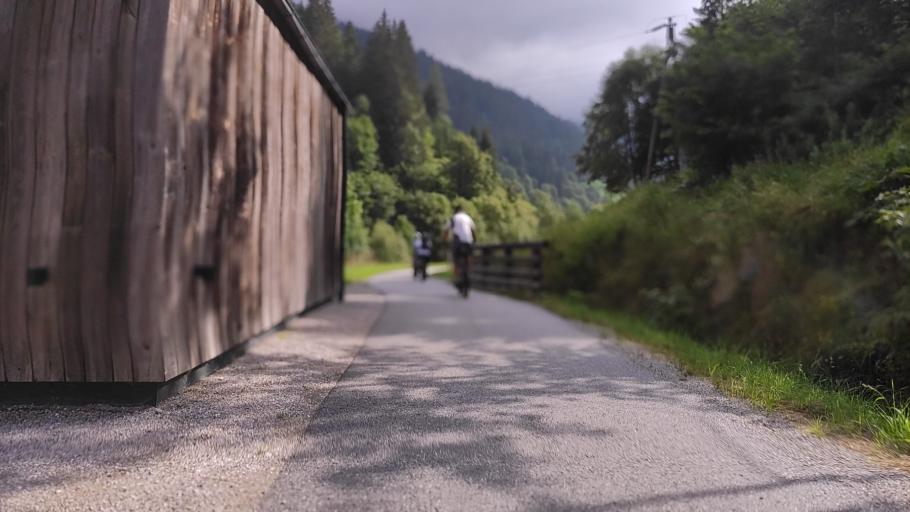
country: AT
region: Salzburg
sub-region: Politischer Bezirk Zell am See
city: Viehhofen
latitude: 47.3629
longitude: 12.7559
